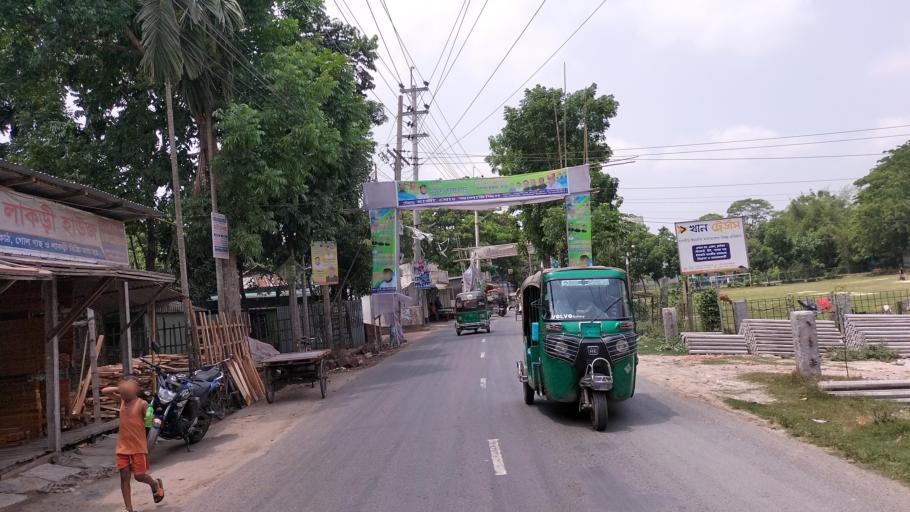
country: BD
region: Dhaka
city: Azimpur
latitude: 23.7296
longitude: 90.2808
